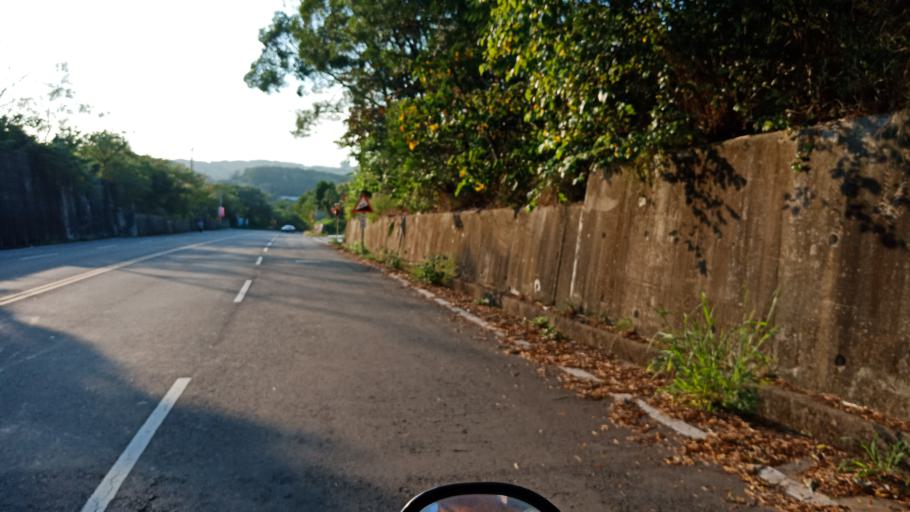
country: TW
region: Taiwan
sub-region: Hsinchu
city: Hsinchu
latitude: 24.7605
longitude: 120.9978
